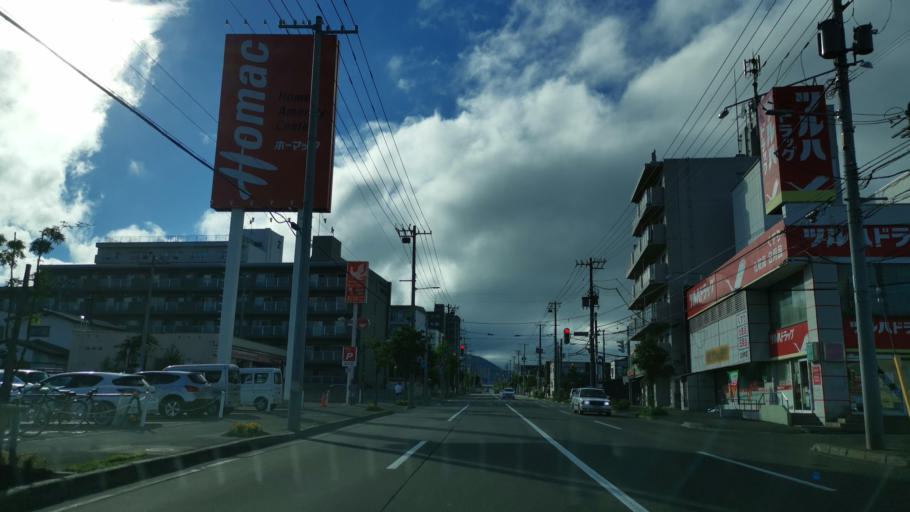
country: JP
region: Hokkaido
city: Sapporo
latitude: 43.0657
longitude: 141.2988
